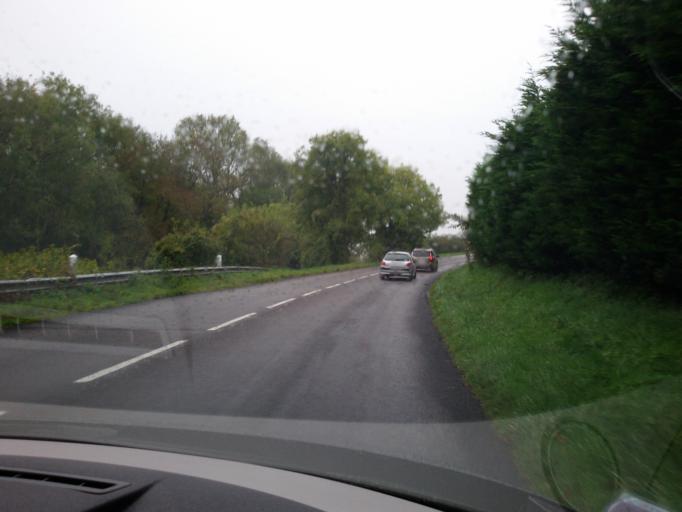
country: FR
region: Lower Normandy
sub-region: Departement du Calvados
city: Villers-sur-Mer
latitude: 49.3090
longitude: -0.0165
